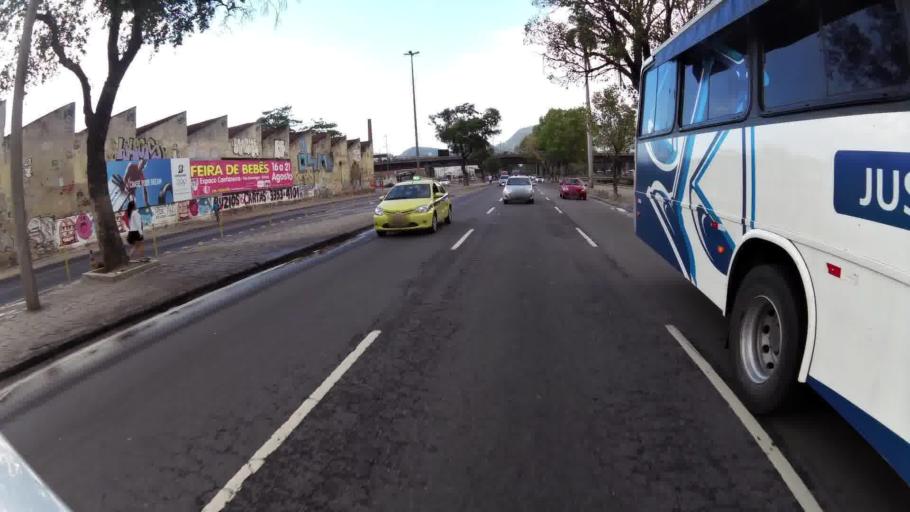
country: BR
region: Rio de Janeiro
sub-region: Rio De Janeiro
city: Rio de Janeiro
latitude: -22.9051
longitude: -43.2096
